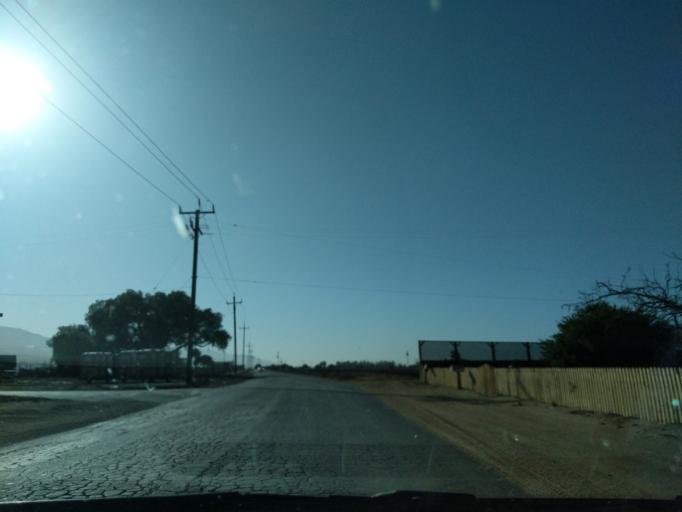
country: US
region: California
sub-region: Monterey County
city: Soledad
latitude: 36.4006
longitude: -121.3404
